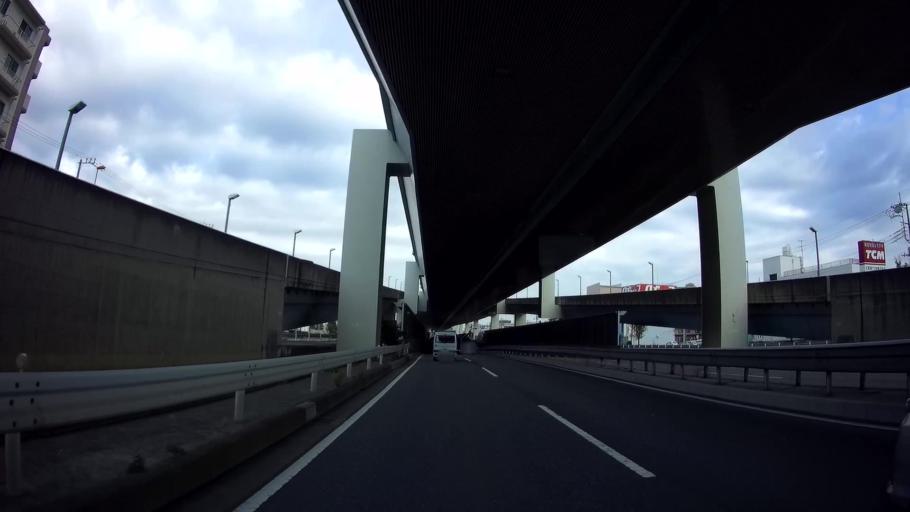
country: JP
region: Saitama
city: Yono
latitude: 35.8672
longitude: 139.6204
